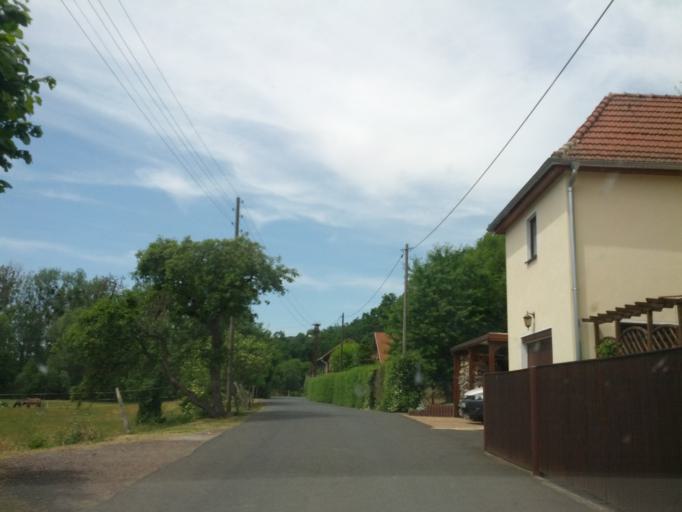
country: DE
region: Thuringia
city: Seebach
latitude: 50.9472
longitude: 10.4290
